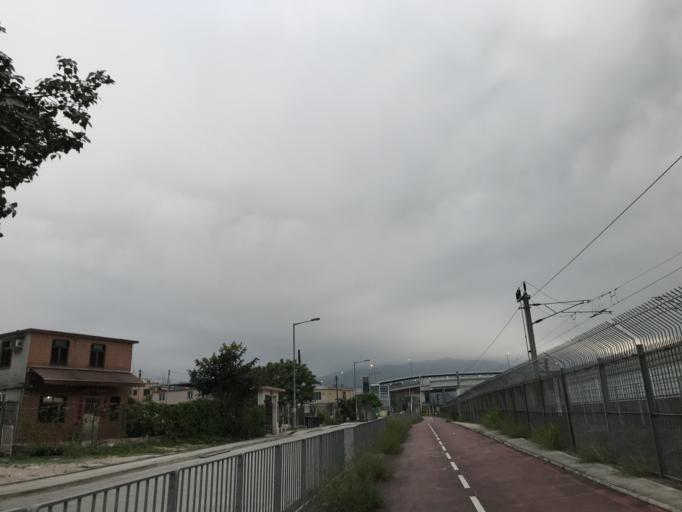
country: HK
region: Tai Po
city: Tai Po
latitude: 22.4770
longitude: 114.1548
